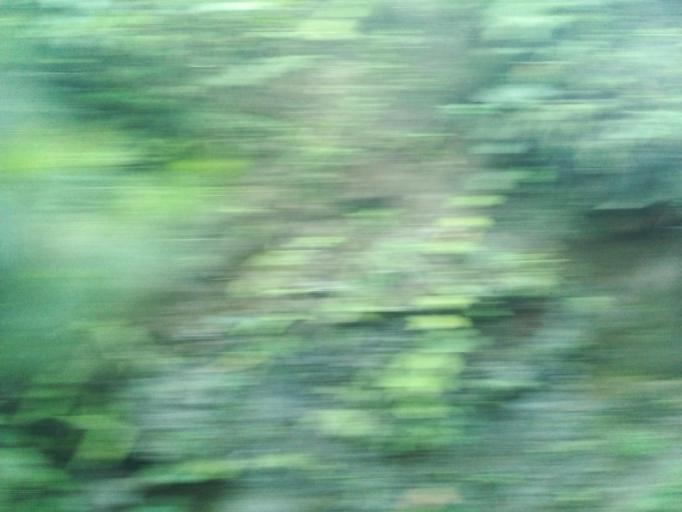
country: BR
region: Minas Gerais
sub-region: Nova Era
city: Nova Era
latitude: -19.7752
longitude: -43.0718
